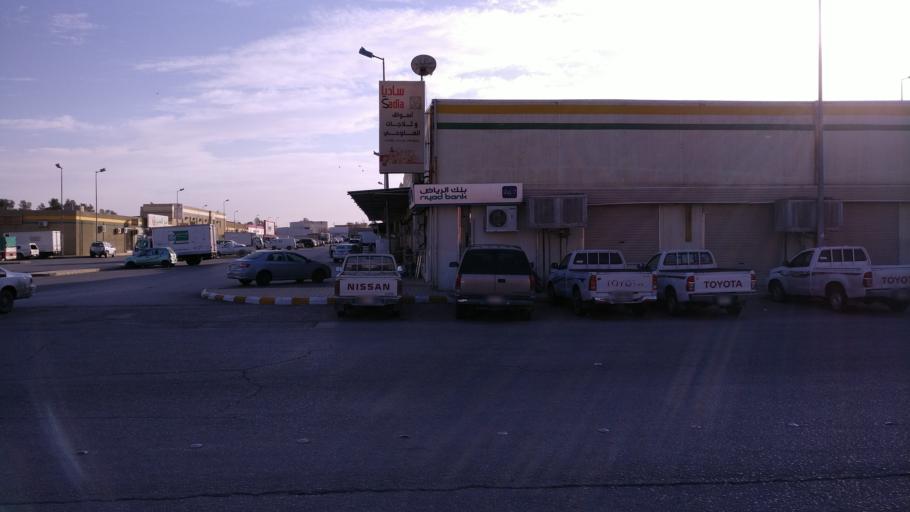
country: SA
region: Al-Qassim
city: Unaizah
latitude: 26.0873
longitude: 43.9660
